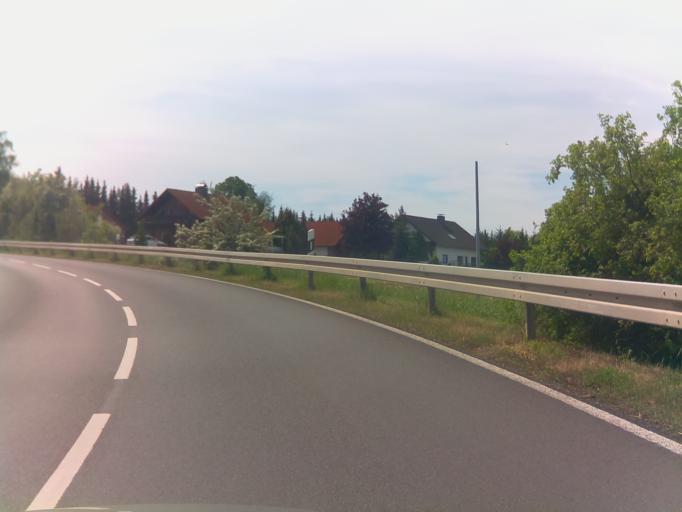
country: DE
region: Saxony-Anhalt
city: Kroppenstedt
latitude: 51.9377
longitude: 11.3059
